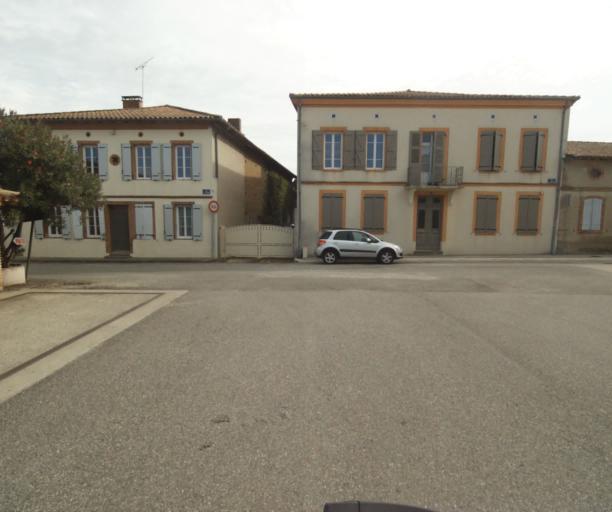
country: FR
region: Midi-Pyrenees
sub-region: Departement du Tarn-et-Garonne
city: Finhan
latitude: 43.9128
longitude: 1.2202
